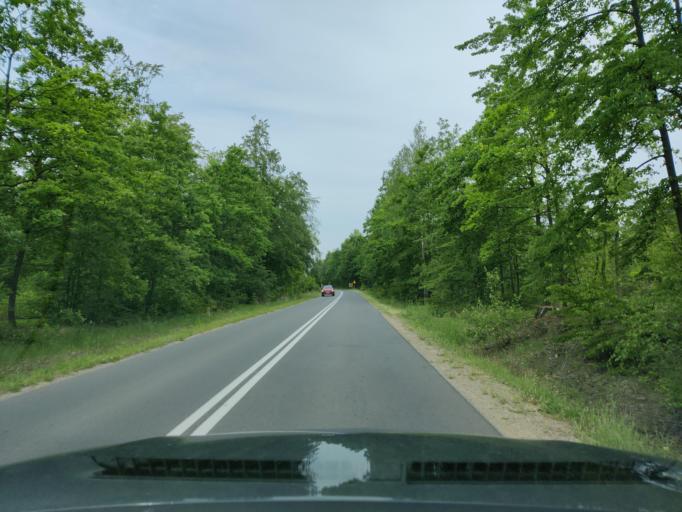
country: PL
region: Masovian Voivodeship
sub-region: Powiat wyszkowski
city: Rzasnik
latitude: 52.6799
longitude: 21.4200
